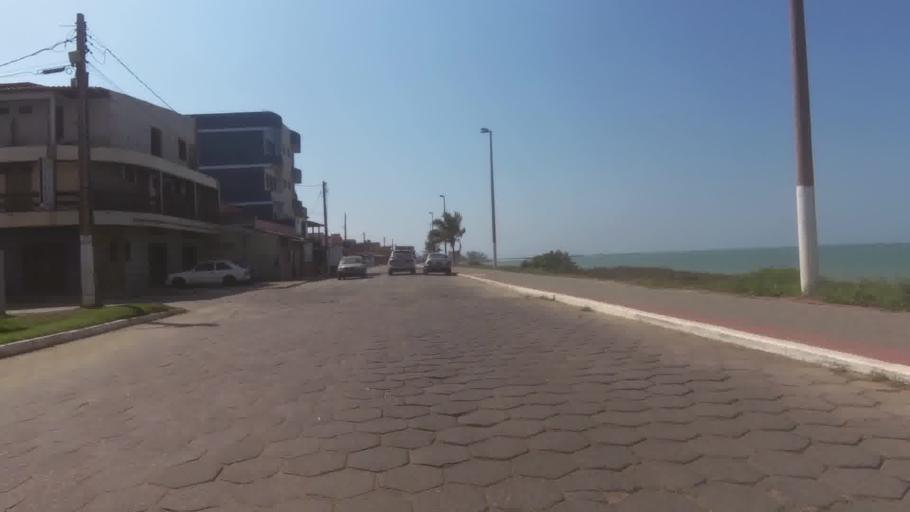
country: BR
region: Espirito Santo
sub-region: Itapemirim
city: Itapemirim
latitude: -21.0160
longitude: -40.8098
